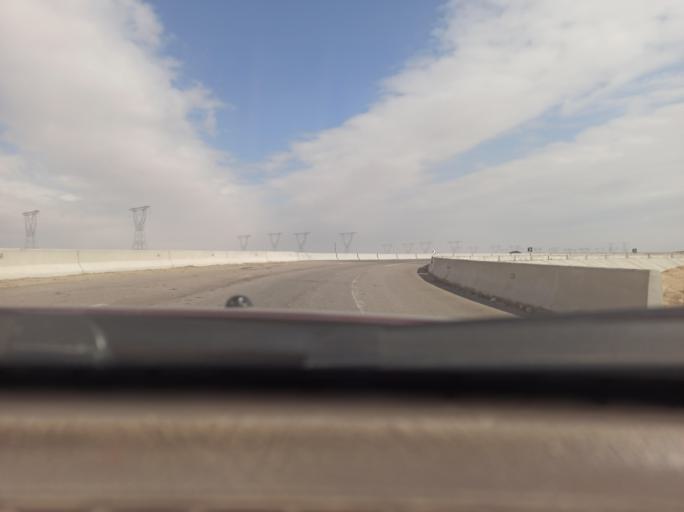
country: EG
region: Muhafazat al Fayyum
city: Tamiyah
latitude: 29.6443
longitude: 31.0128
